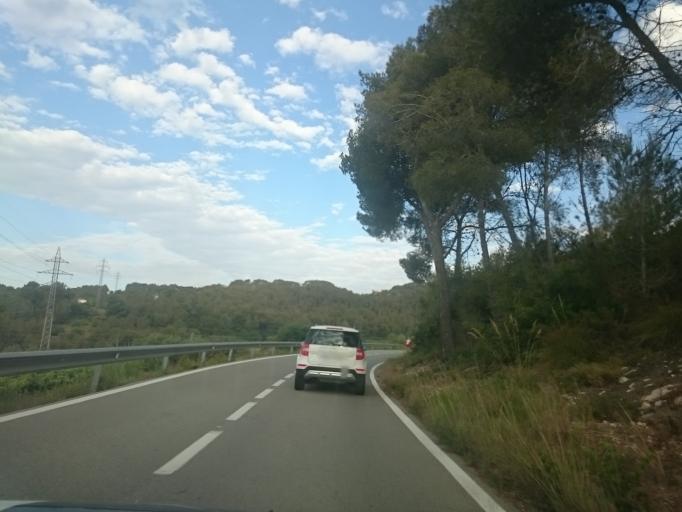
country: ES
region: Catalonia
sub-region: Provincia de Barcelona
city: Cubelles
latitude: 41.2327
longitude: 1.6672
